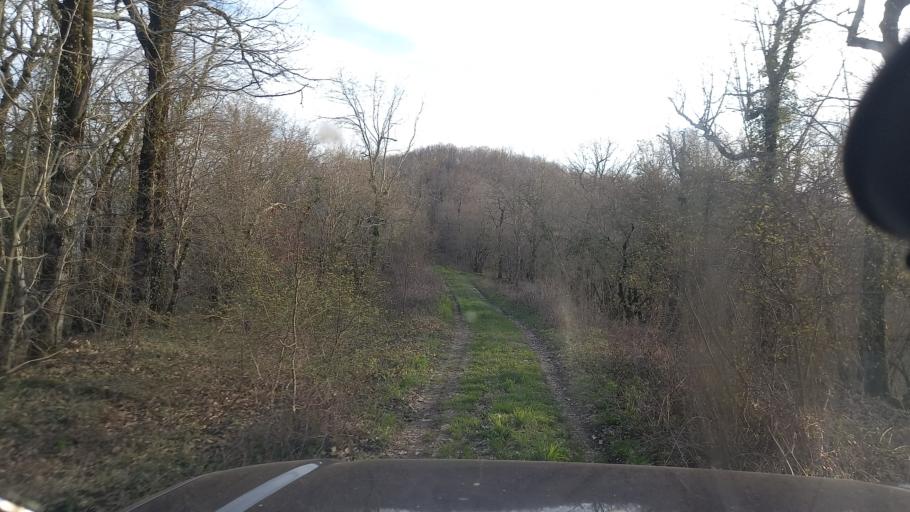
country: RU
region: Krasnodarskiy
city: Arkhipo-Osipovka
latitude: 44.3593
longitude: 38.5533
